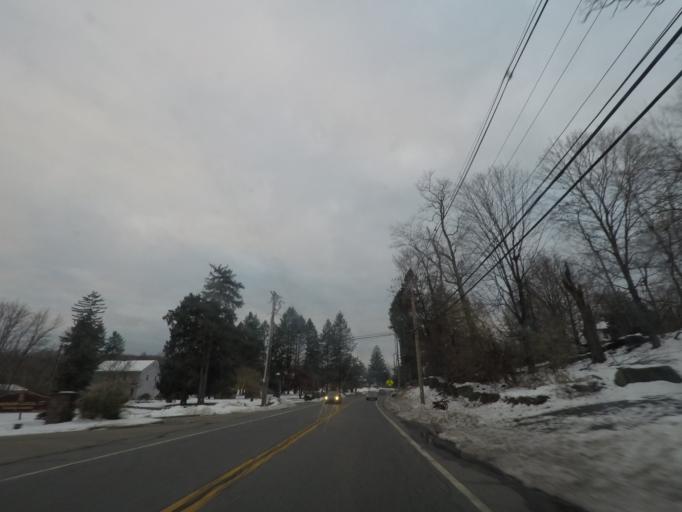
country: US
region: New York
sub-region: Orange County
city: New Windsor
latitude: 41.4939
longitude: -74.0490
